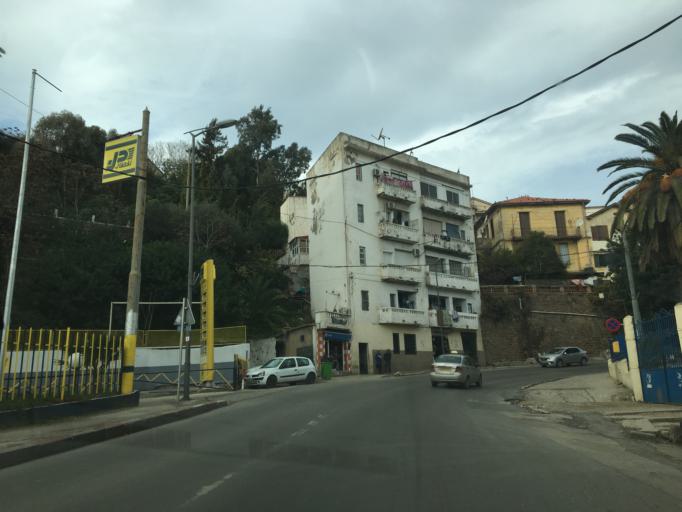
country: DZ
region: Alger
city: Algiers
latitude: 36.7734
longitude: 3.0429
